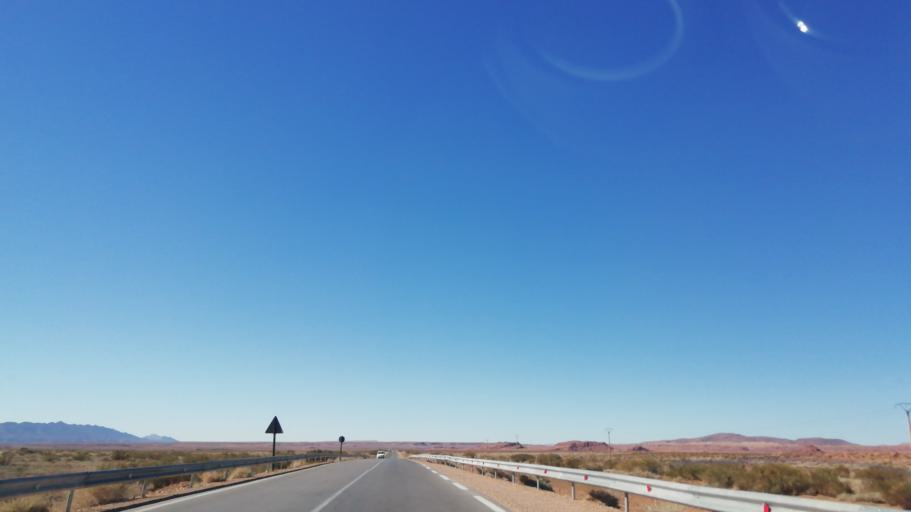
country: DZ
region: El Bayadh
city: El Abiodh Sidi Cheikh
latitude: 33.1840
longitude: 0.5580
